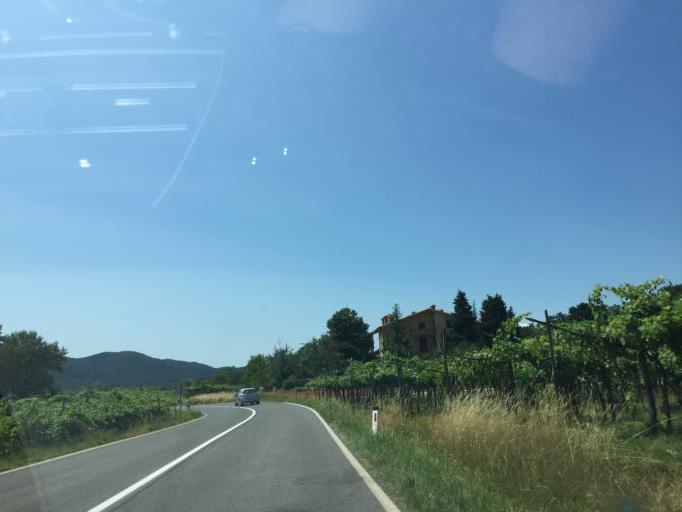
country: IT
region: Friuli Venezia Giulia
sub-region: Provincia di Trieste
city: Zolla
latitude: 45.7560
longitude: 13.8412
